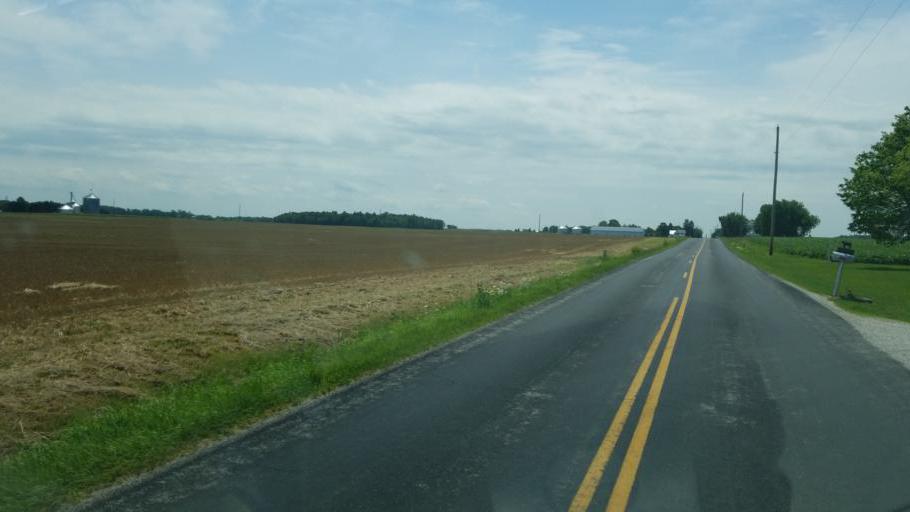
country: US
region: Ohio
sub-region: Crawford County
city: Bucyrus
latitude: 40.8735
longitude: -82.9018
